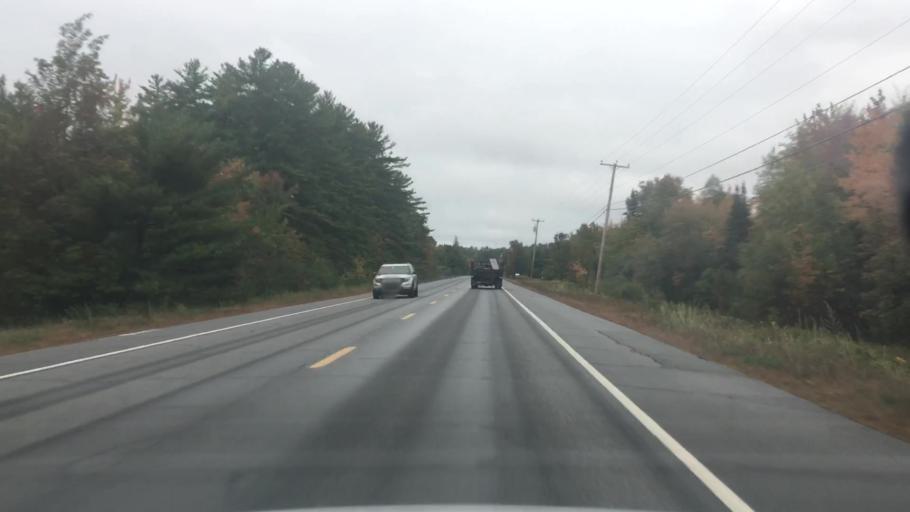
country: US
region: Maine
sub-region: Kennebec County
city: Belgrade
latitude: 44.4284
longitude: -69.8312
